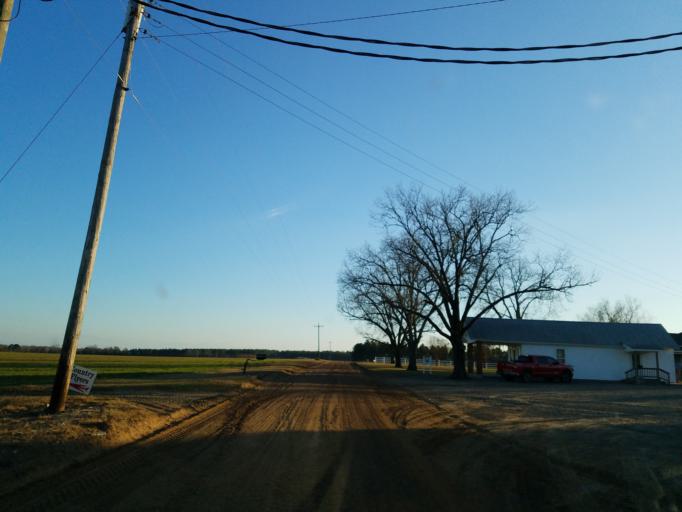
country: US
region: Georgia
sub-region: Worth County
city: Sylvester
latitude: 31.6028
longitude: -83.7868
